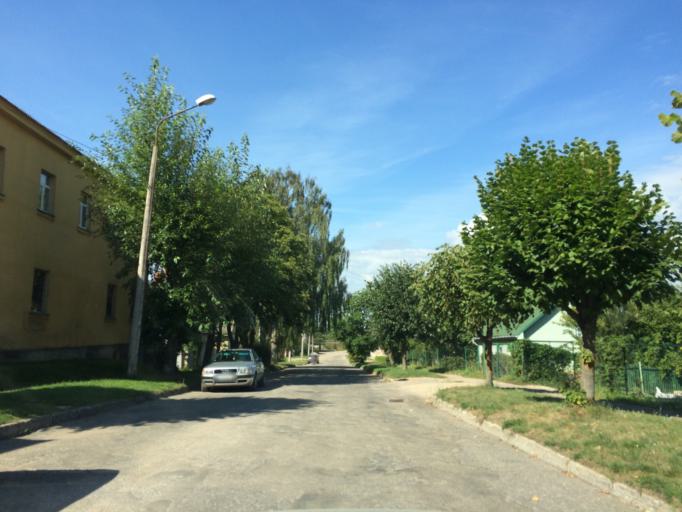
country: LV
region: Rezekne
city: Rezekne
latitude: 56.5110
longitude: 27.3252
